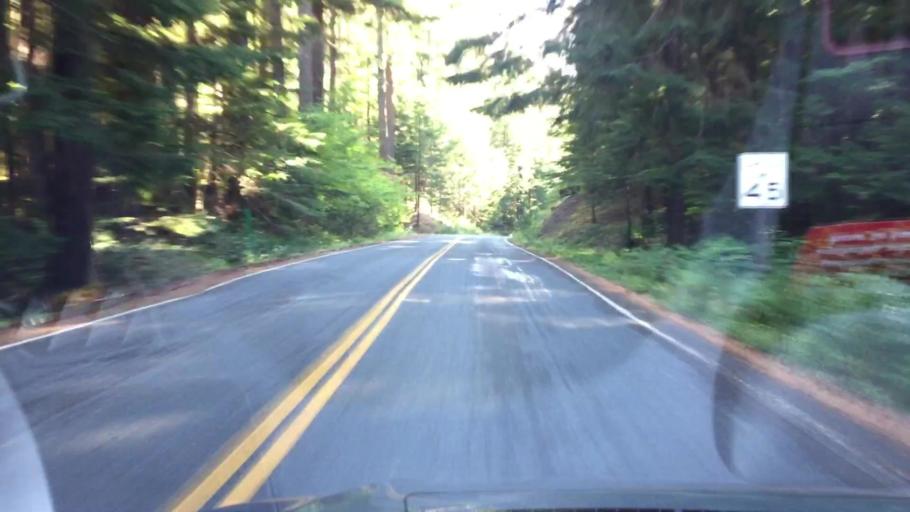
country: US
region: Washington
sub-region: Pierce County
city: Buckley
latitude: 46.7301
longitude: -121.5701
